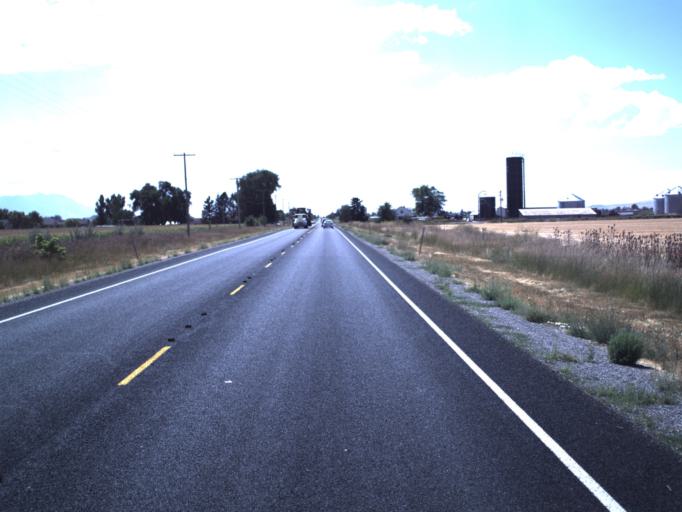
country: US
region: Utah
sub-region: Box Elder County
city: Garland
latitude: 41.7734
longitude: -112.1490
